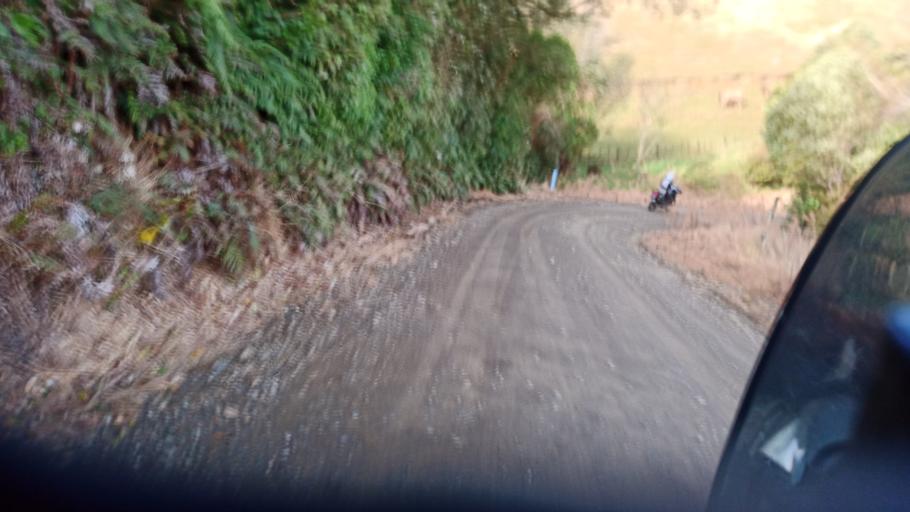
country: NZ
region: Gisborne
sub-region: Gisborne District
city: Gisborne
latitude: -38.4540
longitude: 177.5385
